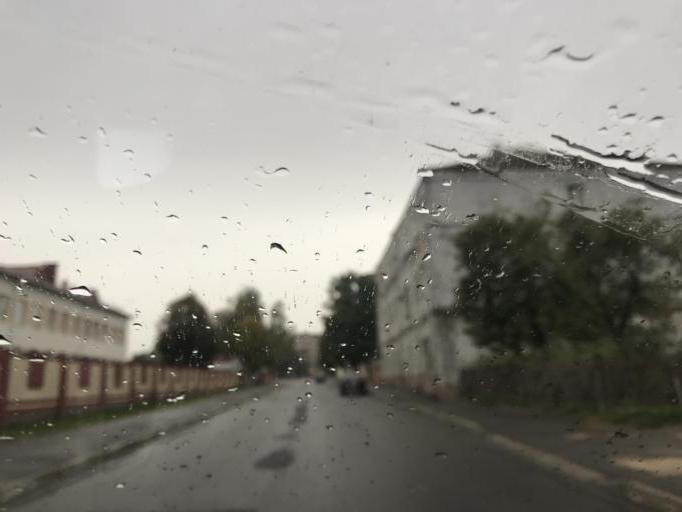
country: BY
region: Mogilev
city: Mahilyow
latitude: 53.8952
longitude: 30.3197
